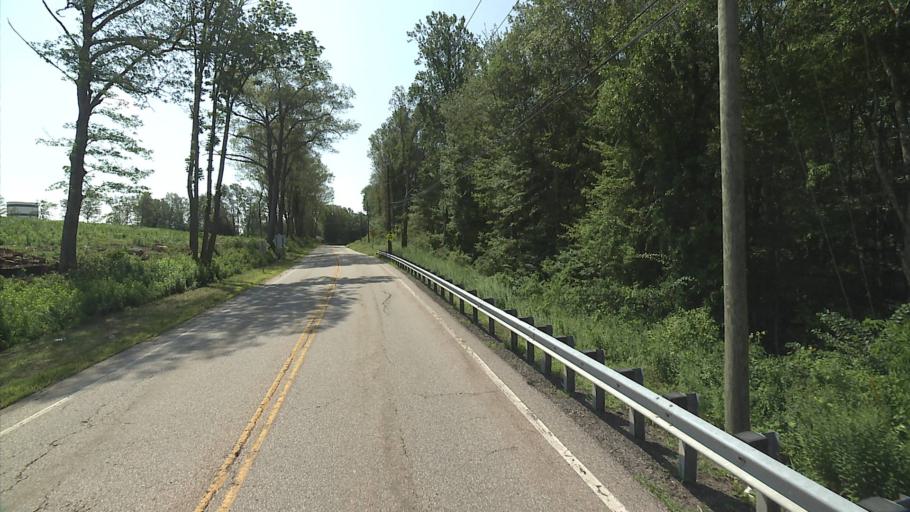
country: US
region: Connecticut
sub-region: New London County
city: Montville Center
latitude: 41.4255
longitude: -72.2149
